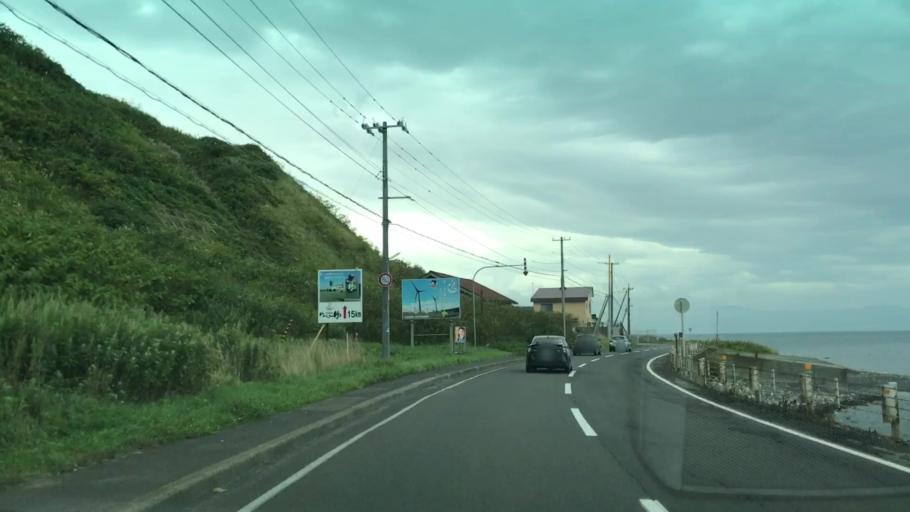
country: JP
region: Hokkaido
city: Iwanai
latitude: 42.8706
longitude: 140.3571
